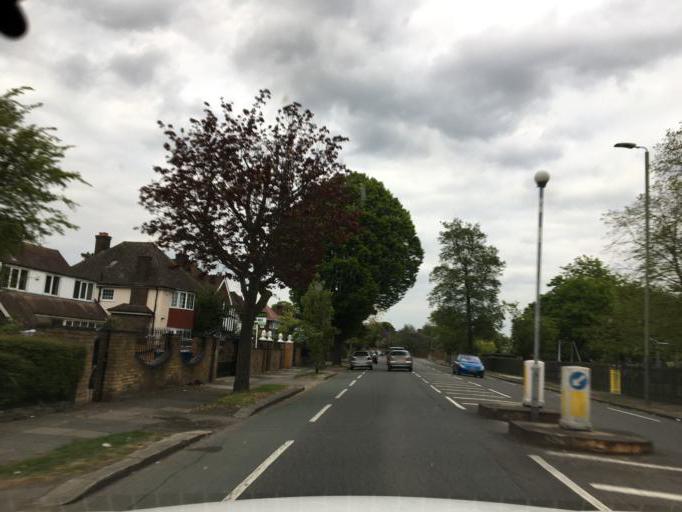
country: GB
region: England
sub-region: Greater London
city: Chislehurst
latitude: 51.4344
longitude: 0.0379
